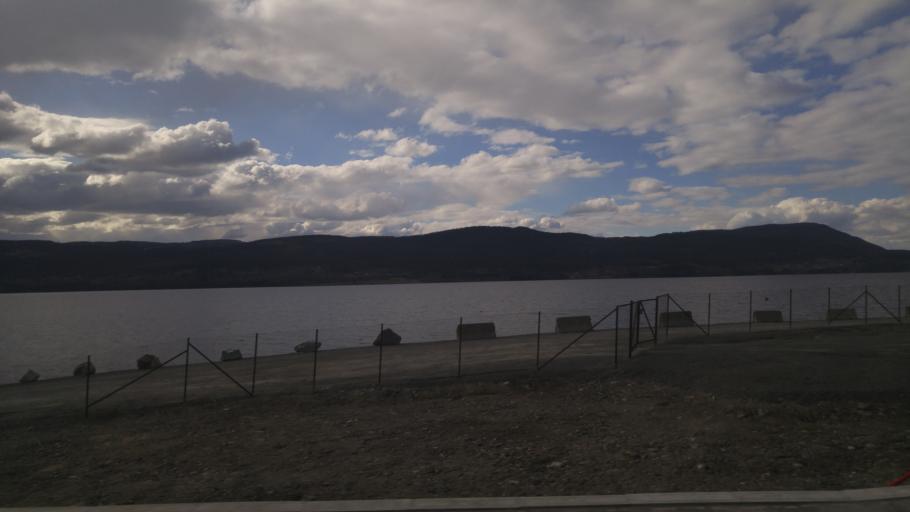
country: NO
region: Akershus
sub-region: Eidsvoll
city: Eidsvoll
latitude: 60.5027
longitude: 11.2365
